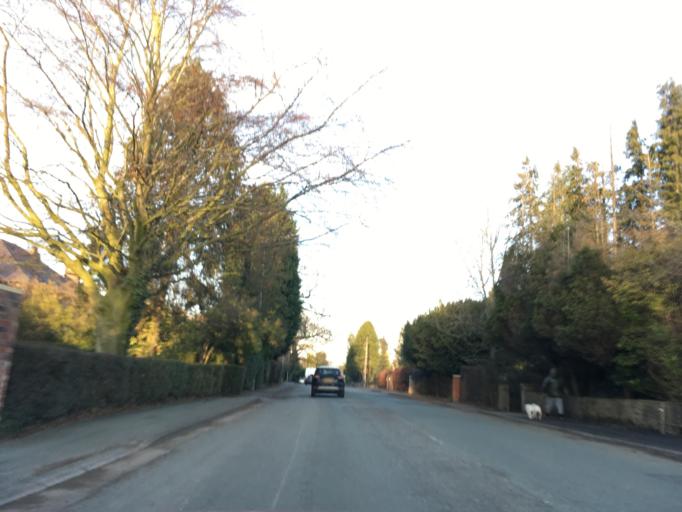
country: GB
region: England
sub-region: Cheshire East
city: Wilmslow
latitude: 53.3403
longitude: -2.2217
